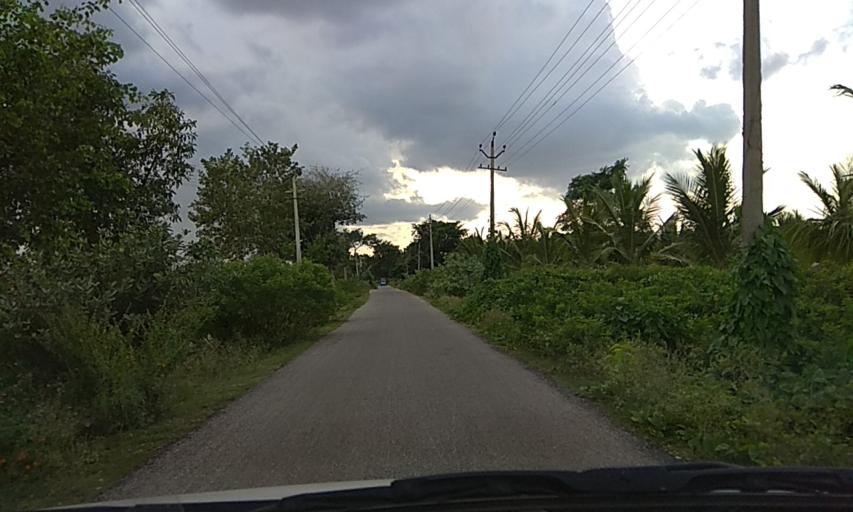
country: IN
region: Karnataka
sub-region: Chamrajnagar
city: Gundlupet
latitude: 11.8713
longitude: 76.7456
